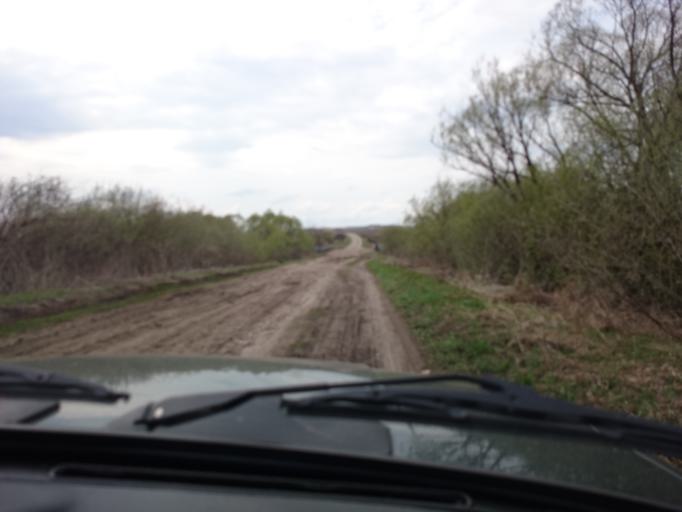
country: RU
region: Mordoviya
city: Kadoshkino
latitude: 54.0180
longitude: 44.4565
